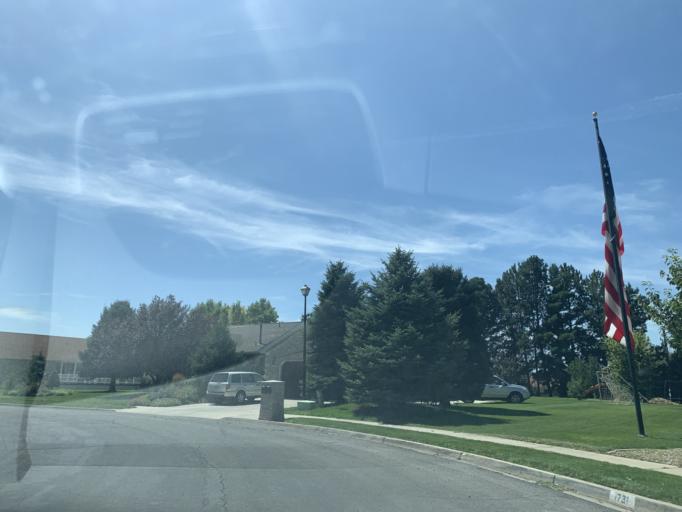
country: US
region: Utah
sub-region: Utah County
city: Lehi
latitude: 40.4097
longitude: -111.8276
